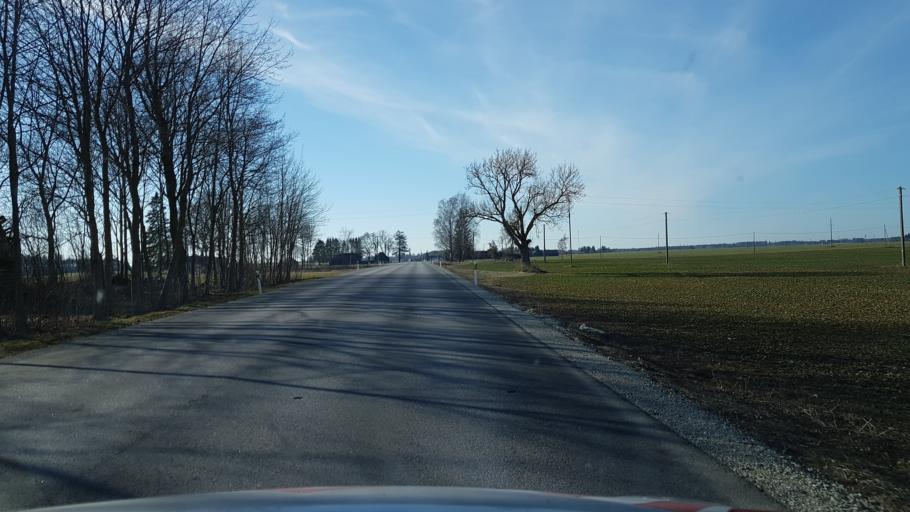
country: EE
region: Laeaene-Virumaa
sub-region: Vinni vald
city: Vinni
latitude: 59.2336
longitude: 26.5047
